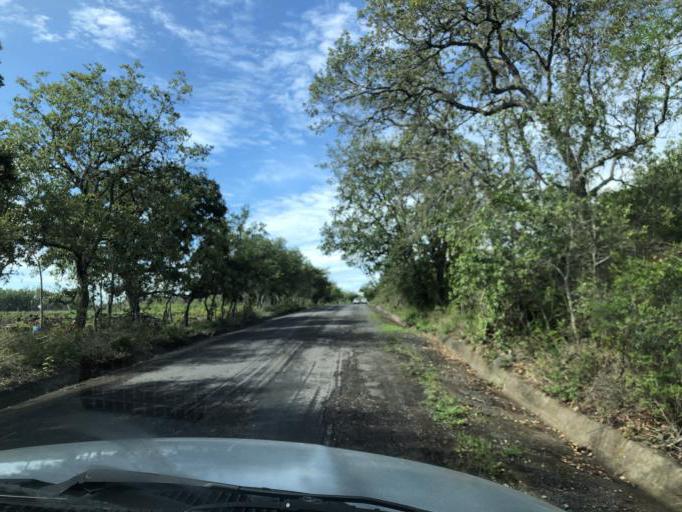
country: MX
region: Veracruz
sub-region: Alto Lucero de Gutierrez Barrios
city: Palma Sola
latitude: 19.7960
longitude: -96.5476
